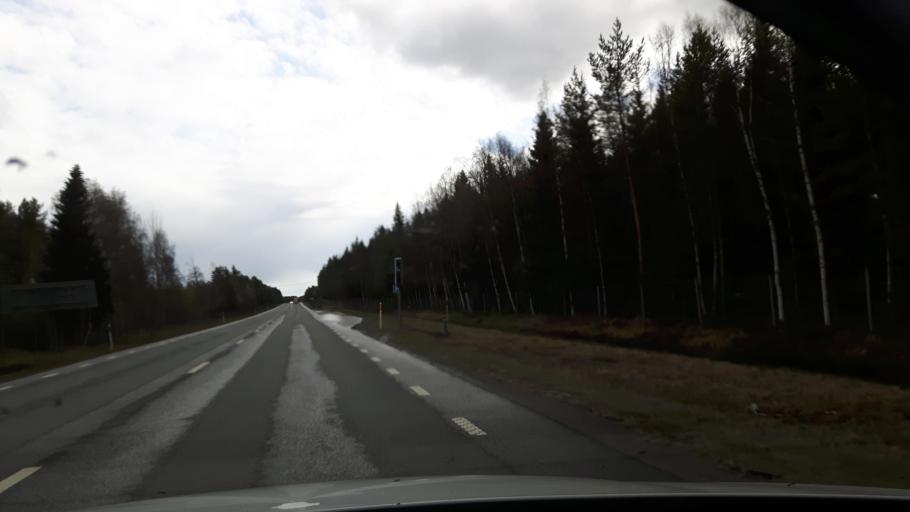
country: SE
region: Vaesterbotten
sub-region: Robertsfors Kommun
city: Robertsfors
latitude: 64.0578
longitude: 20.8476
